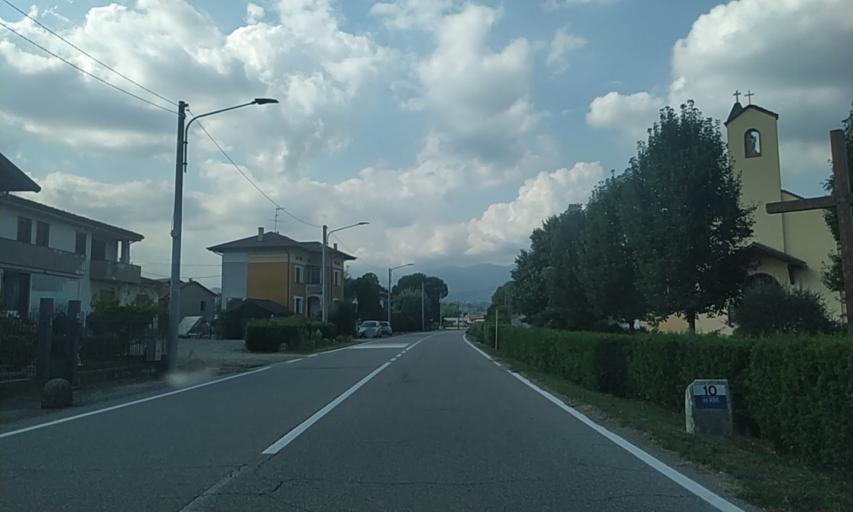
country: IT
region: Piedmont
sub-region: Provincia di Biella
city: Cerreto Castello
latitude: 45.5488
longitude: 8.1754
